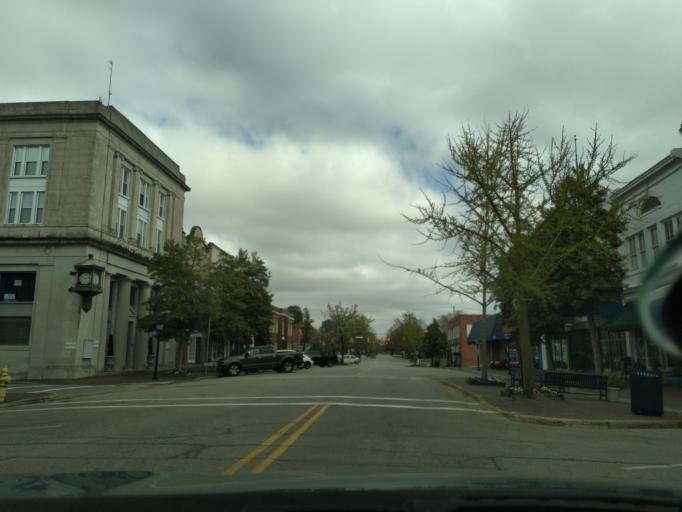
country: US
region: North Carolina
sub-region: Chowan County
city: Edenton
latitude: 36.0587
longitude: -76.6089
